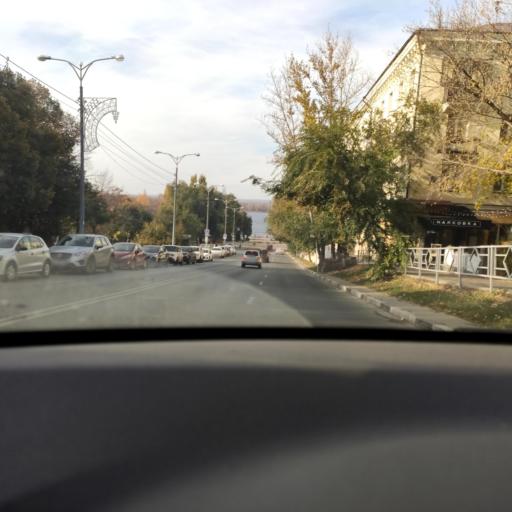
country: RU
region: Samara
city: Samara
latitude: 53.2052
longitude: 50.1129
